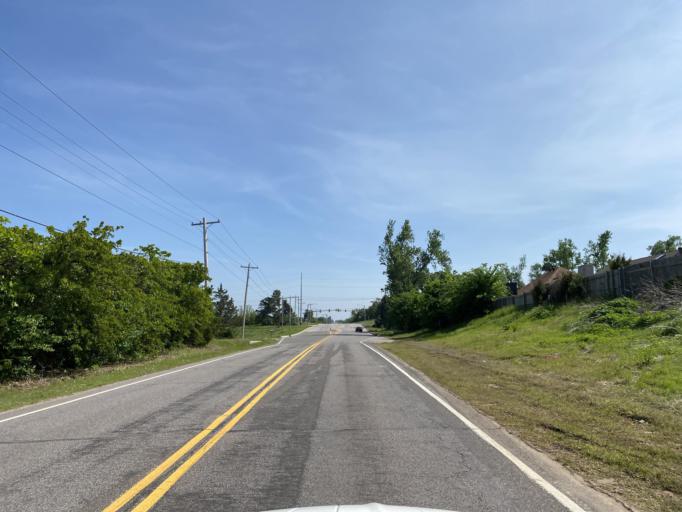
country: US
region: Oklahoma
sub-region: Oklahoma County
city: Nicoma Park
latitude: 35.4523
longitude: -97.3358
